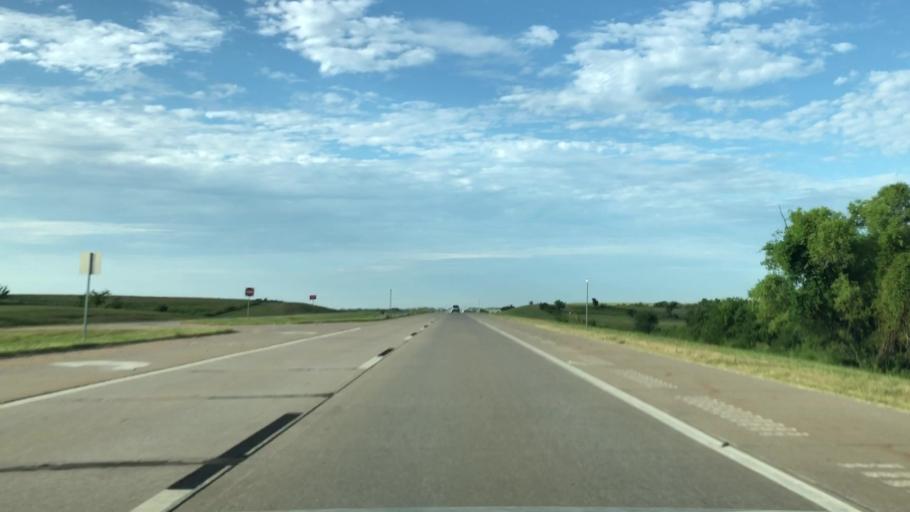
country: US
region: Oklahoma
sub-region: Osage County
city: Skiatook
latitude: 36.4096
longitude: -95.9206
